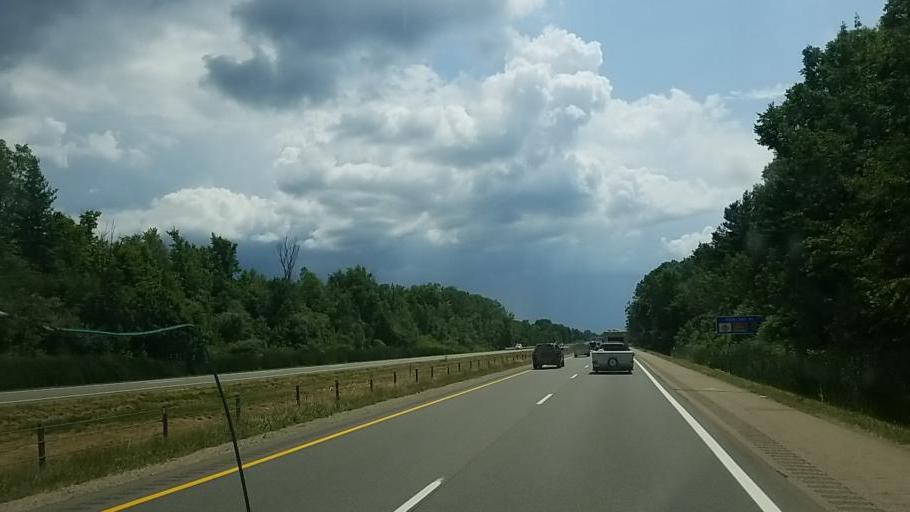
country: US
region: Michigan
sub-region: Kent County
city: Northview
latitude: 42.9969
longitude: -85.6050
